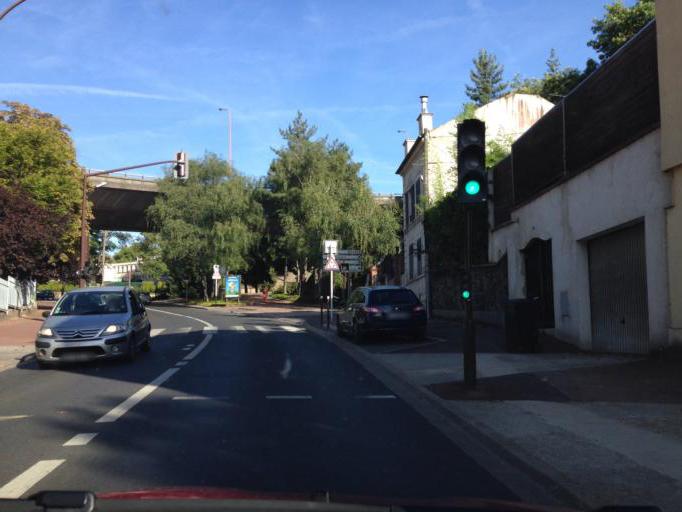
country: FR
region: Ile-de-France
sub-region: Departement des Hauts-de-Seine
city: Sevres
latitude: 48.8232
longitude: 2.2213
